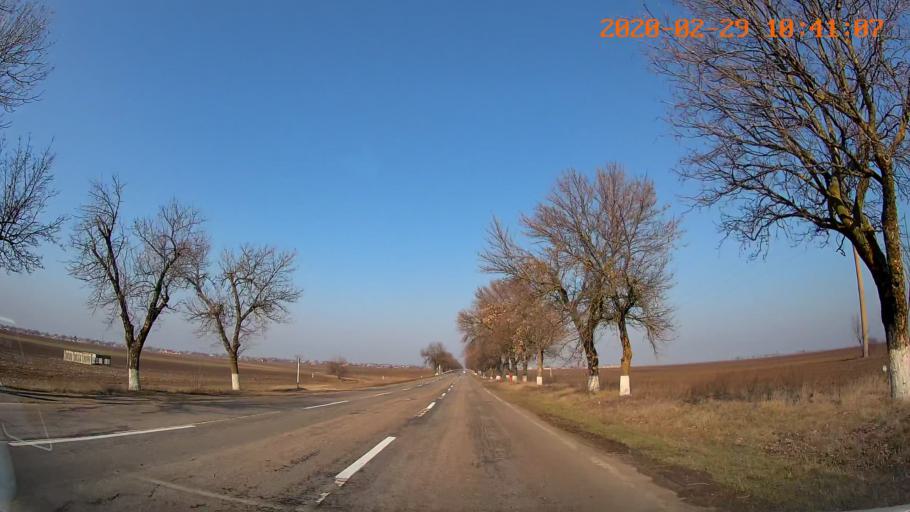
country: MD
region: Telenesti
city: Grigoriopol
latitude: 47.0394
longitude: 29.4299
